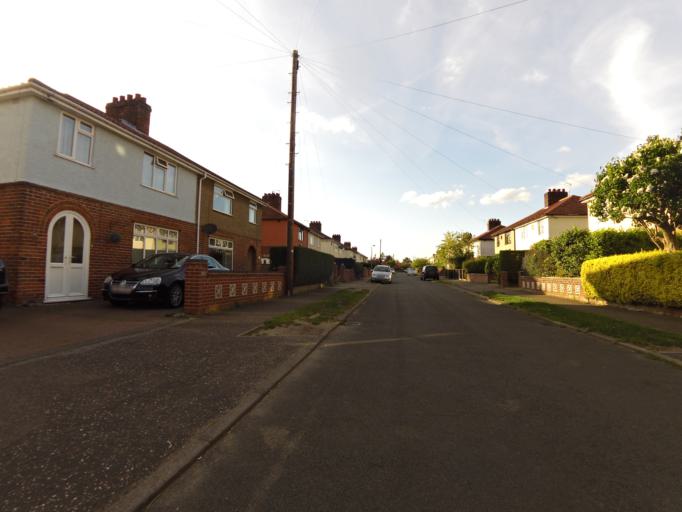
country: GB
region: England
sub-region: Norfolk
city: Norwich
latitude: 52.6566
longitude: 1.2724
